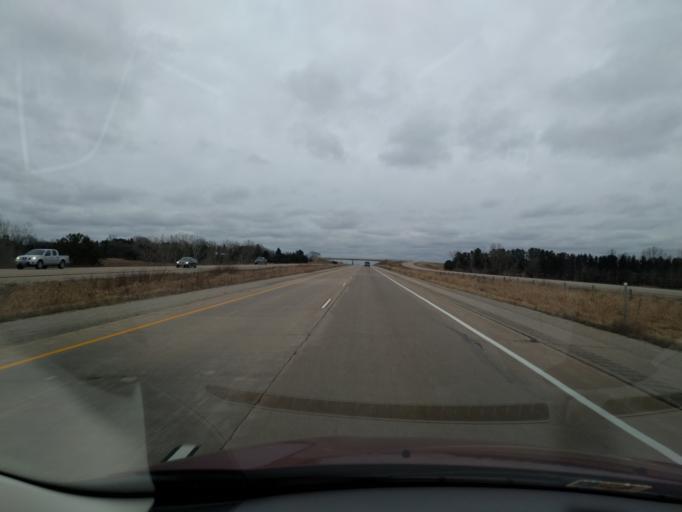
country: US
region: Wisconsin
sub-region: Winnebago County
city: Winneconne
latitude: 44.1884
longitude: -88.6703
